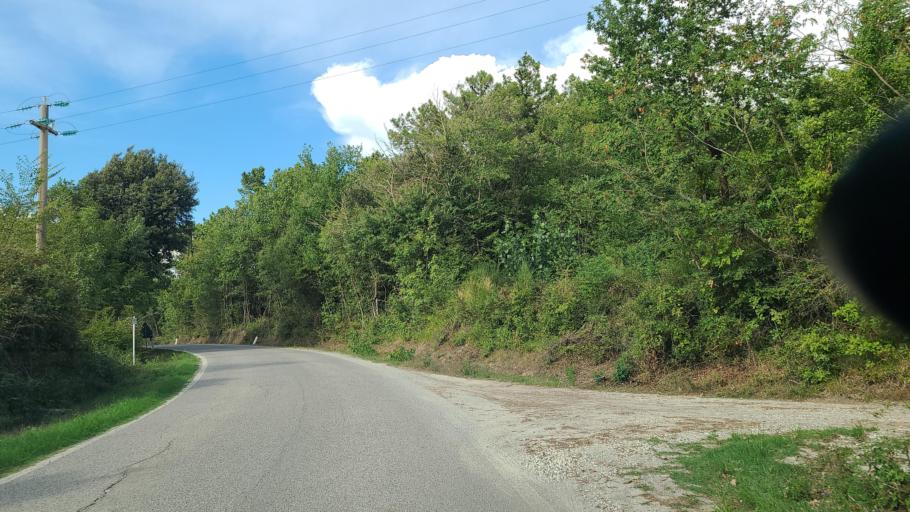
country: IT
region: Tuscany
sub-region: Provincia di Siena
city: San Gimignano
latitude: 43.4137
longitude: 10.9773
